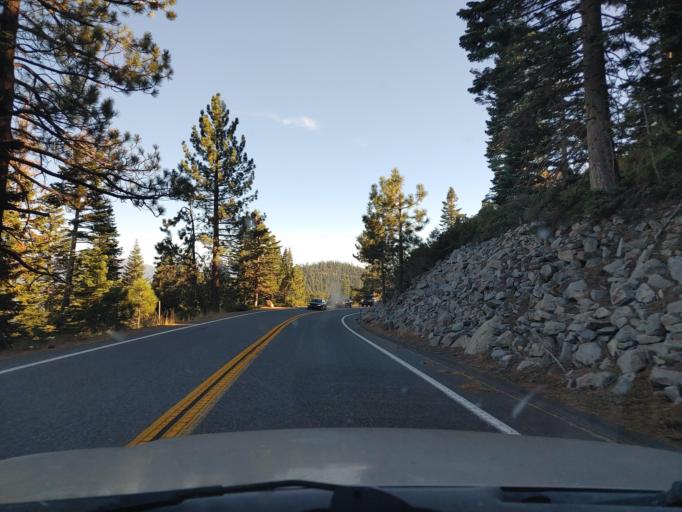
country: US
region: California
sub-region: Placer County
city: Tahoma
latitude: 39.0130
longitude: -120.1177
